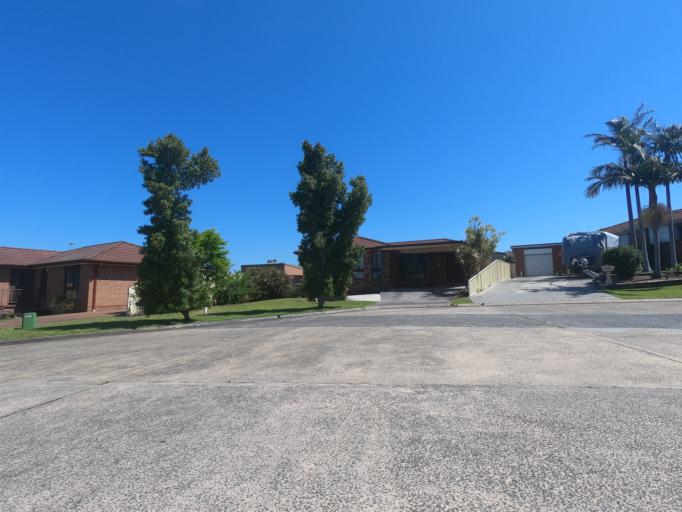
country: AU
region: New South Wales
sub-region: Wollongong
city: Dapto
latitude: -34.4863
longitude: 150.7804
